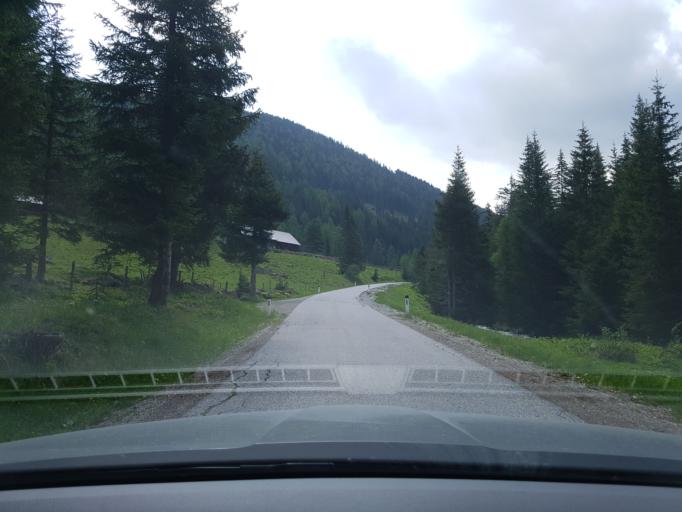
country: AT
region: Salzburg
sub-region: Politischer Bezirk Tamsweg
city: Thomatal
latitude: 47.0283
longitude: 13.7592
